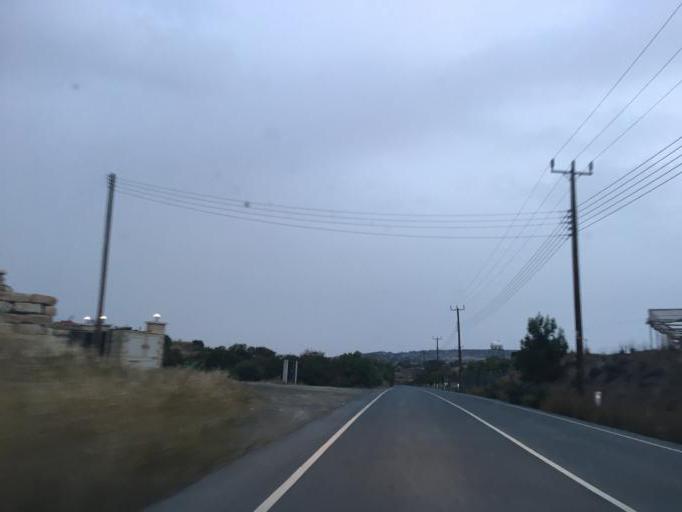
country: CY
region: Limassol
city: Parekklisha
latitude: 34.7631
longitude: 33.1615
